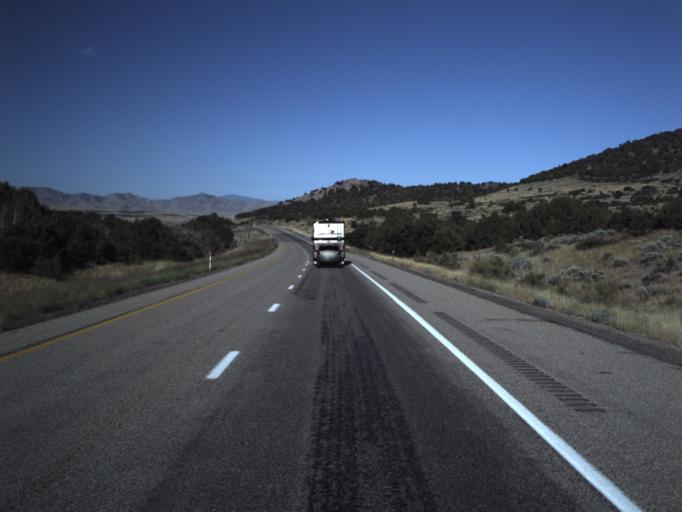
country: US
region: Utah
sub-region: Beaver County
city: Beaver
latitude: 38.6082
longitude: -112.5150
